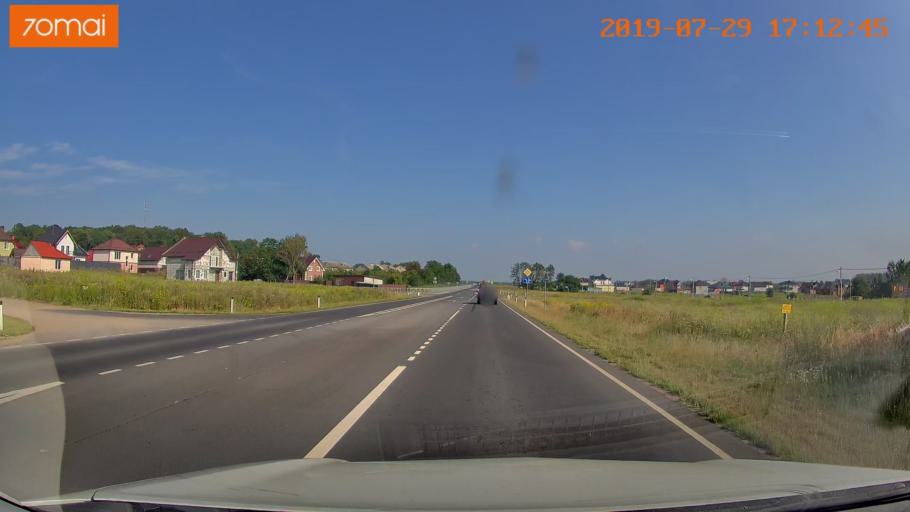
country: RU
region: Kaliningrad
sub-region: Gorod Kaliningrad
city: Kaliningrad
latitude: 54.7866
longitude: 20.4020
